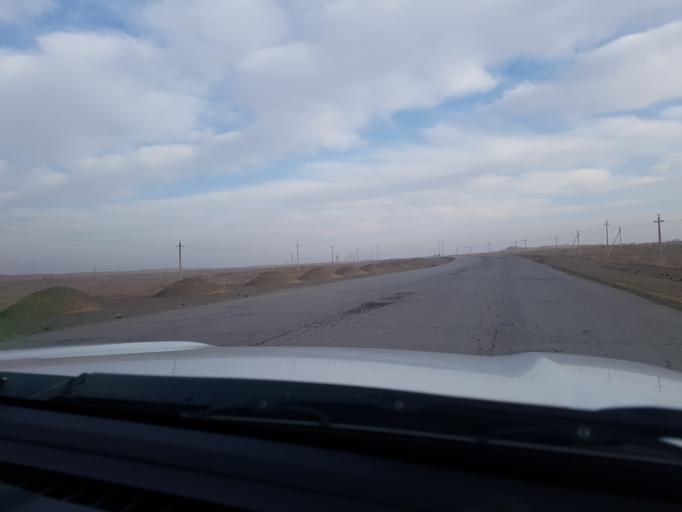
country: TM
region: Ahal
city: Abadan
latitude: 38.7366
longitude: 58.4950
